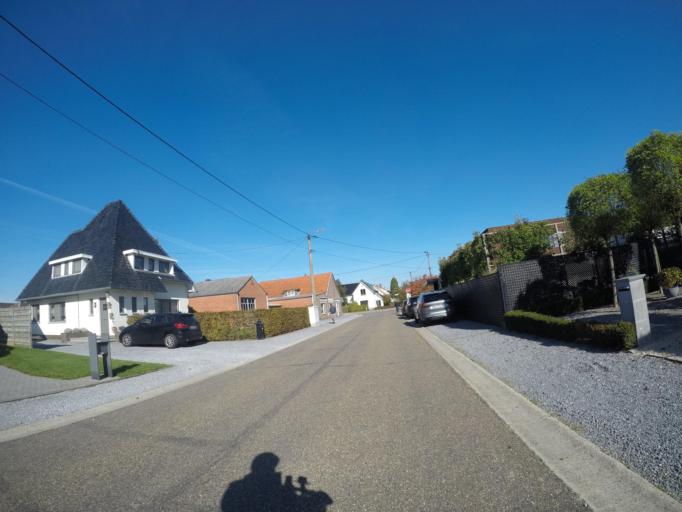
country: BE
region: Flanders
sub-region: Provincie Limburg
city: Alken
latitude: 50.8999
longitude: 5.2705
